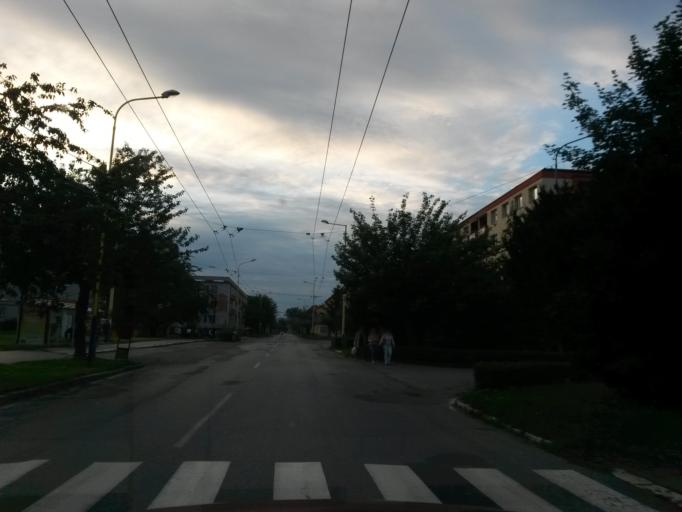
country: SK
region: Presovsky
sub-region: Okres Presov
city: Presov
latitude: 48.9897
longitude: 21.2360
